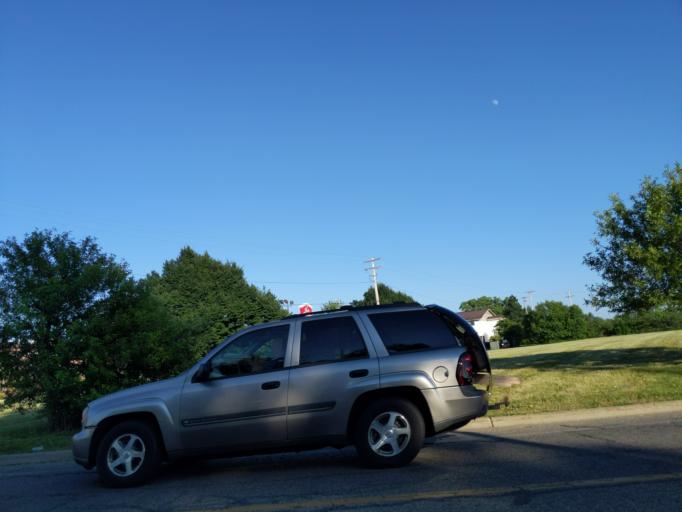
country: US
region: Michigan
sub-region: Ingham County
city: Holt
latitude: 42.6613
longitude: -84.5412
